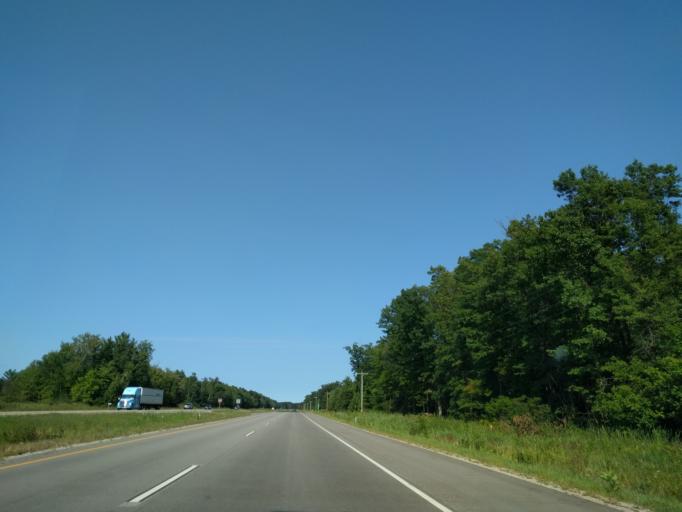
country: US
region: Wisconsin
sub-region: Oconto County
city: Oconto
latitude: 44.8413
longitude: -87.9117
